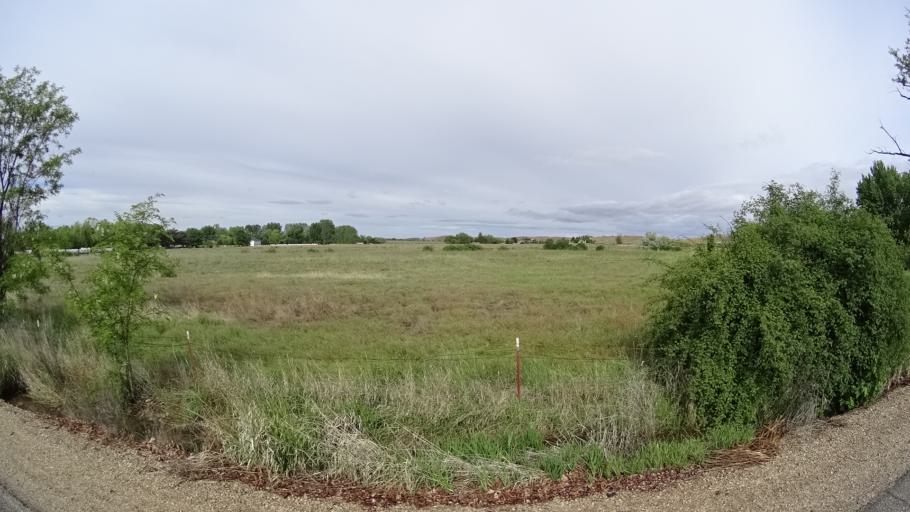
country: US
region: Idaho
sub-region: Ada County
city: Eagle
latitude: 43.7328
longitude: -116.4034
